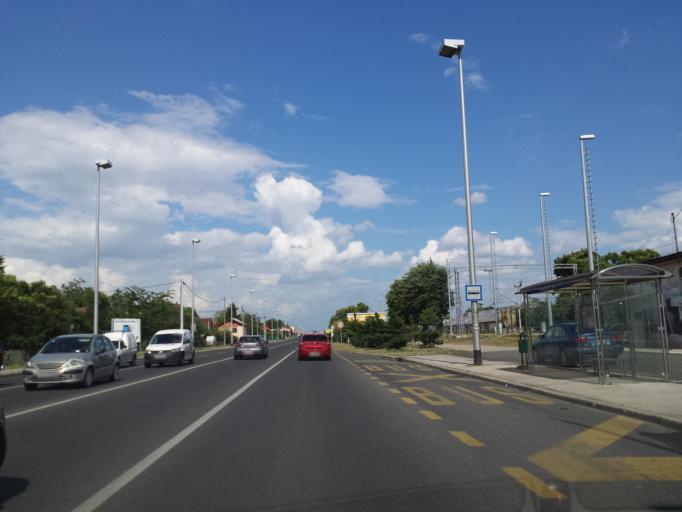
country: HR
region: Grad Zagreb
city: Dubrava
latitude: 45.8186
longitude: 16.0491
